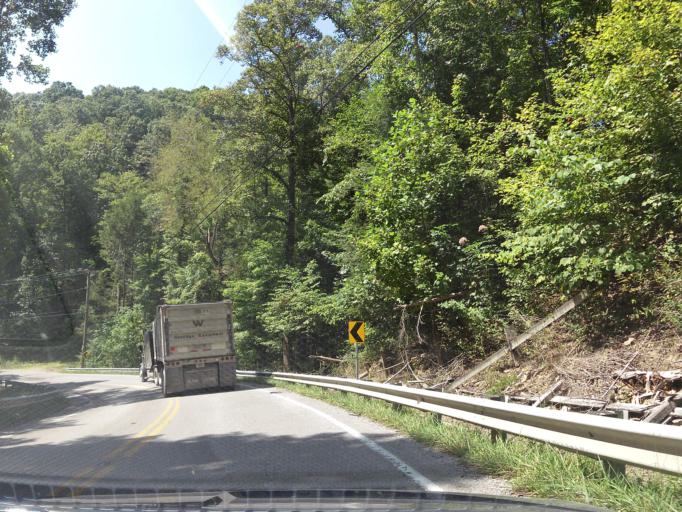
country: US
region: Kentucky
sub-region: Harlan County
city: Harlan
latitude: 36.8769
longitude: -83.3200
